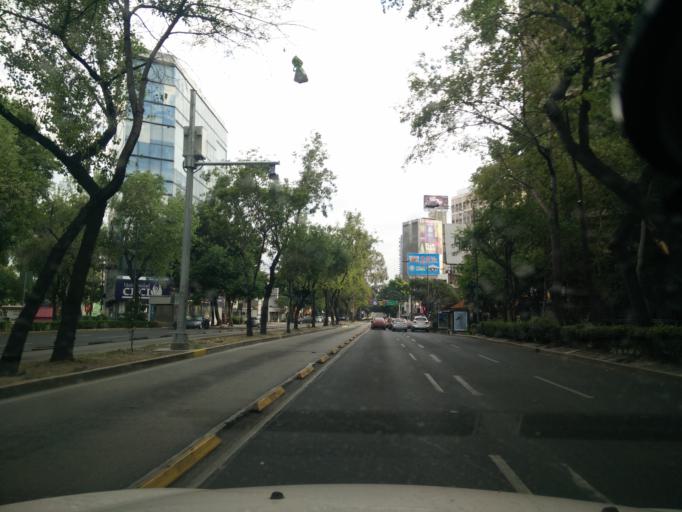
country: MX
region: Mexico City
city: Benito Juarez
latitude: 19.4046
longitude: -99.1691
